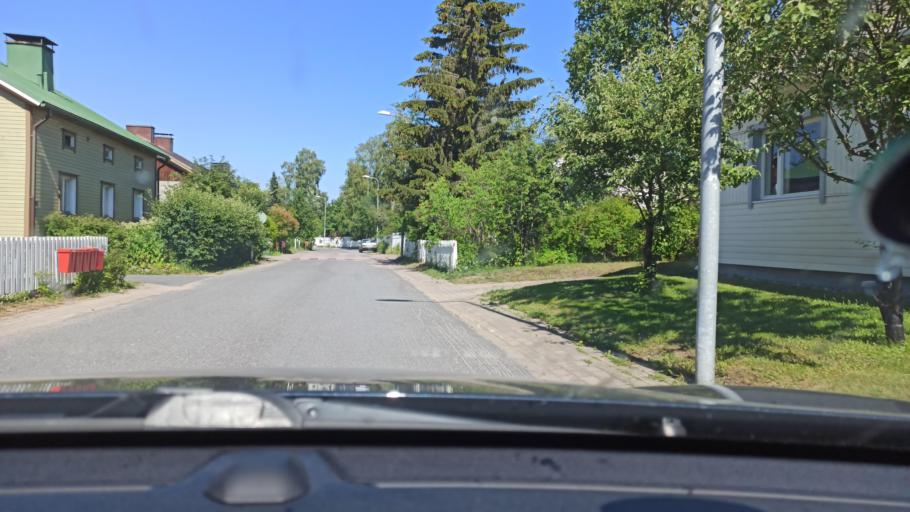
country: FI
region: Northern Ostrobothnia
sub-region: Oulu
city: Oulu
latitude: 65.0400
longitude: 25.4447
